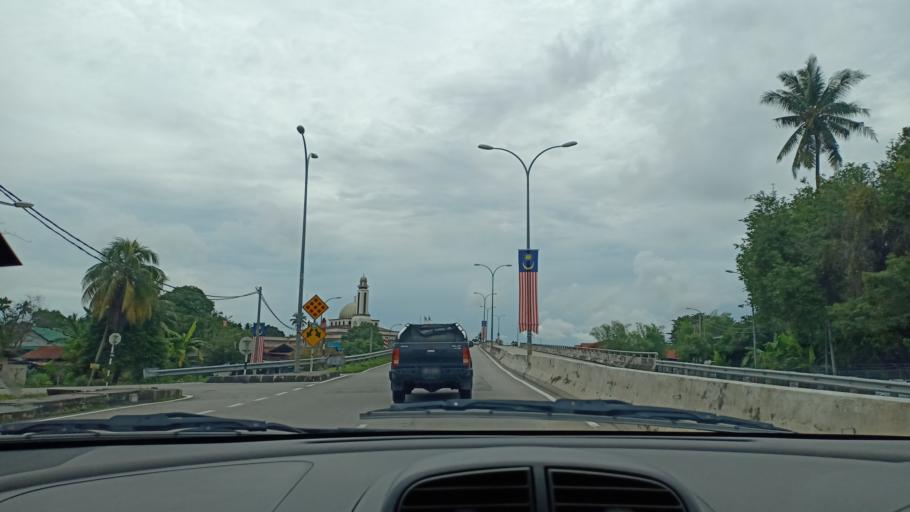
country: MY
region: Penang
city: Bukit Mertajam
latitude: 5.4072
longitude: 100.4752
